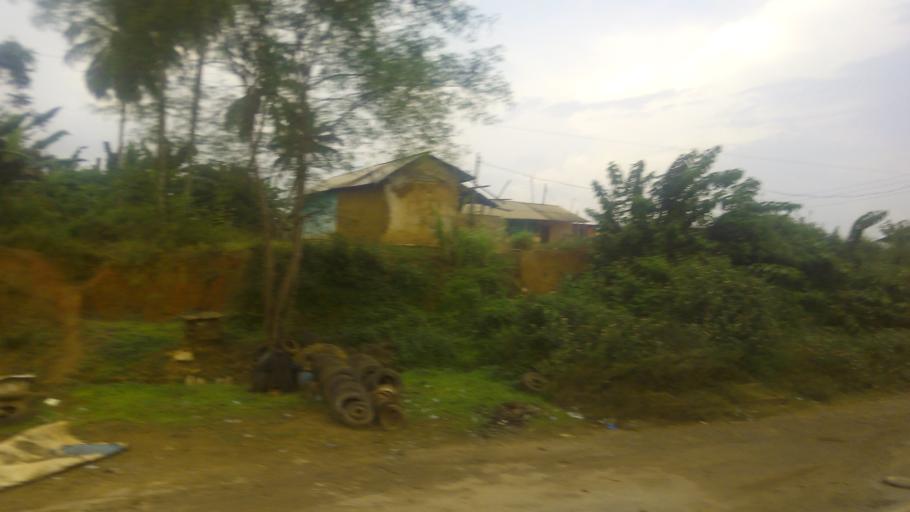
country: GH
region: Western
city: Takoradi
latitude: 4.8922
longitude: -1.8838
